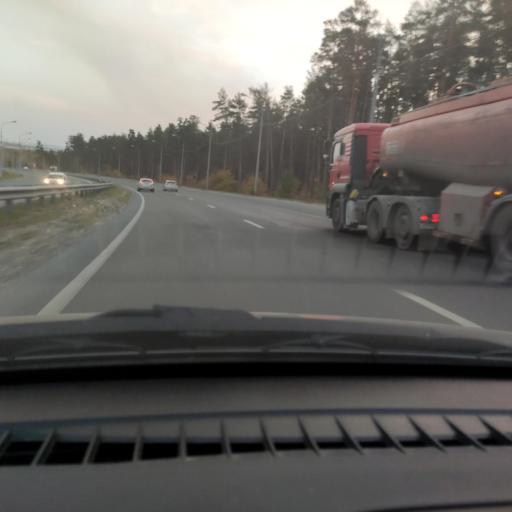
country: RU
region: Samara
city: Zhigulevsk
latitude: 53.5352
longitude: 49.5162
